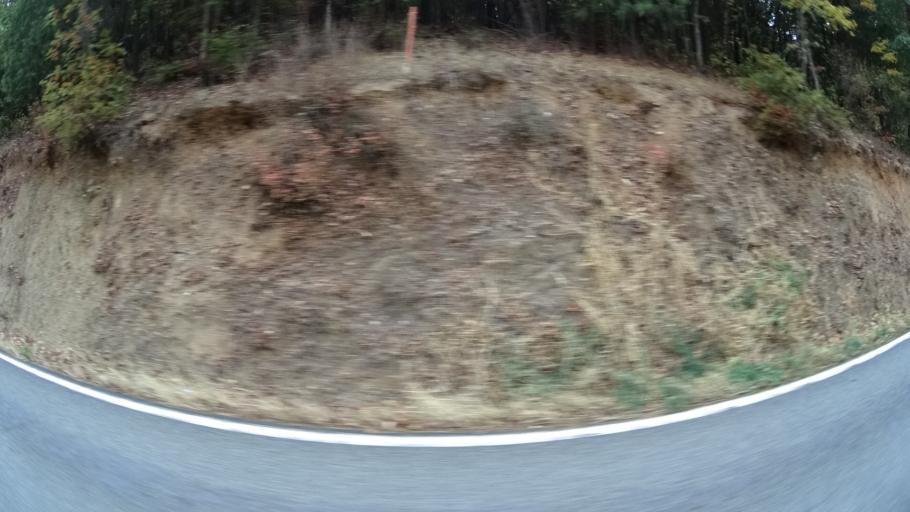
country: US
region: California
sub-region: Siskiyou County
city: Happy Camp
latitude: 41.8572
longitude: -123.3933
